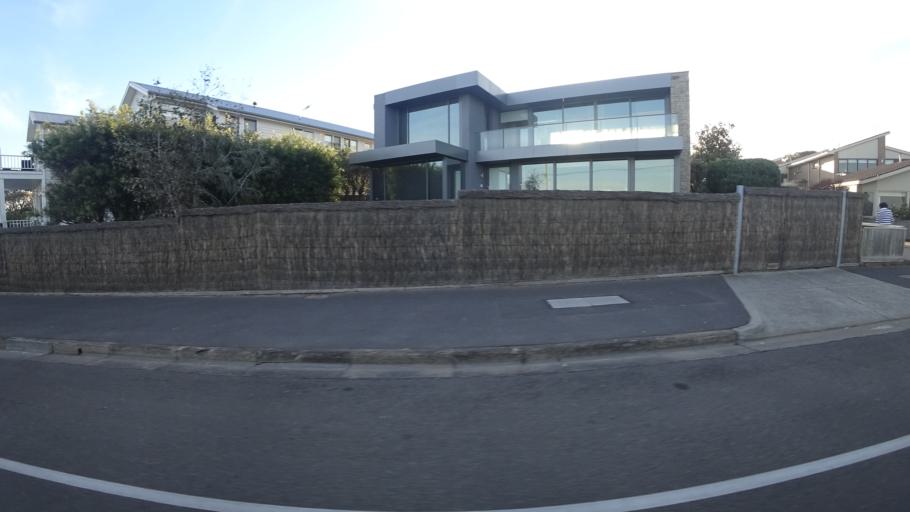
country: AU
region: Victoria
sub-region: Queenscliffe
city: Queenscliff
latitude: -38.2833
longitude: 144.6147
